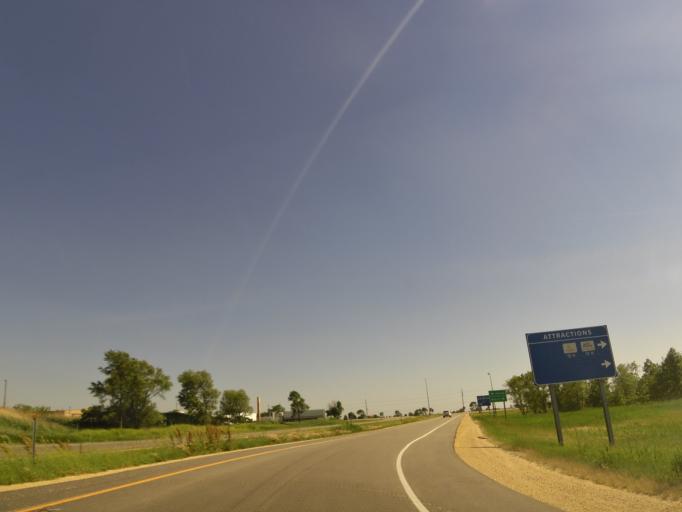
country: US
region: Illinois
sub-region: Ogle County
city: Davis Junction
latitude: 42.1030
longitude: -89.0205
